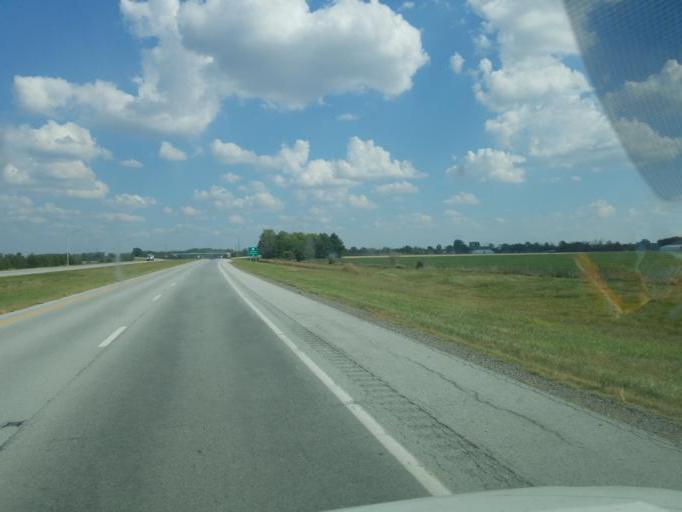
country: US
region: Ohio
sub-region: Allen County
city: Delphos
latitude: 40.8733
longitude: -84.3586
